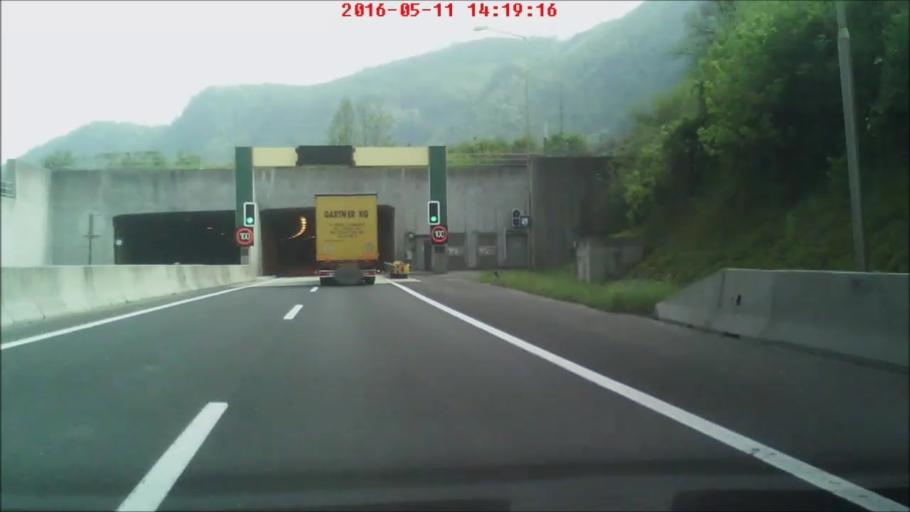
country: AT
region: Upper Austria
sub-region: Politischer Bezirk Kirchdorf an der Krems
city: Micheldorf in Oberoesterreich
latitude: 47.8939
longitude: 14.1047
